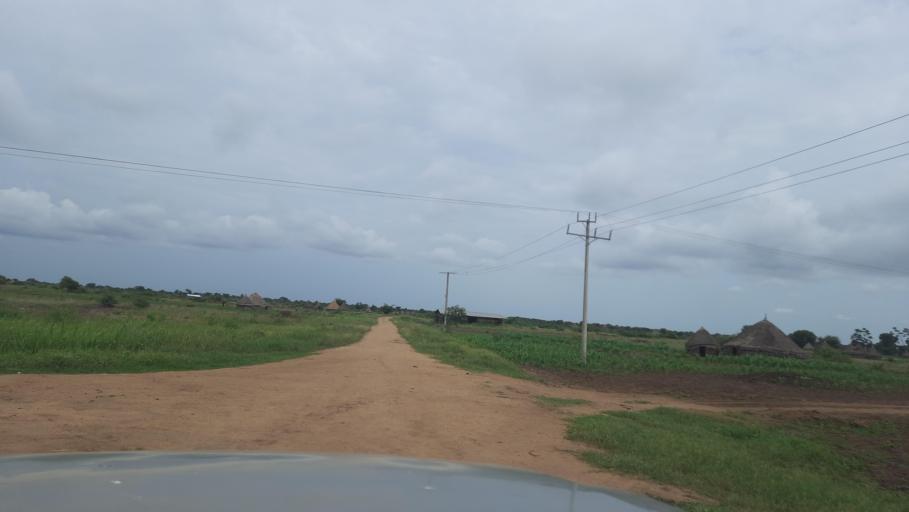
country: ET
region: Gambela
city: Gambela
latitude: 8.3279
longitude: 33.7074
